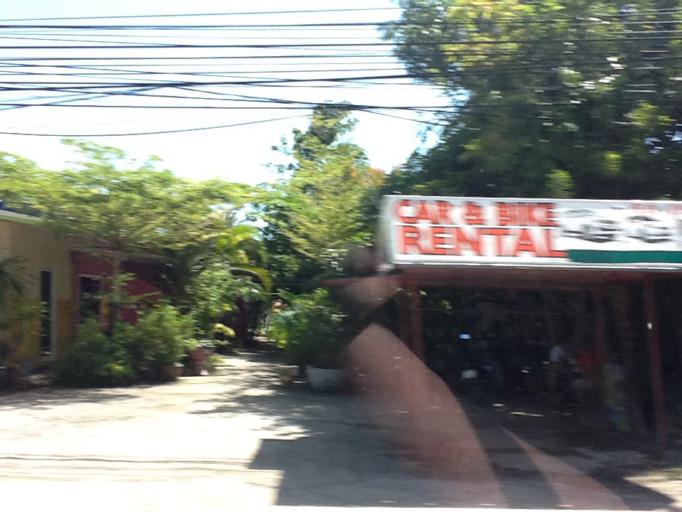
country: TH
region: Phuket
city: Thalang
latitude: 8.0225
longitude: 98.4008
